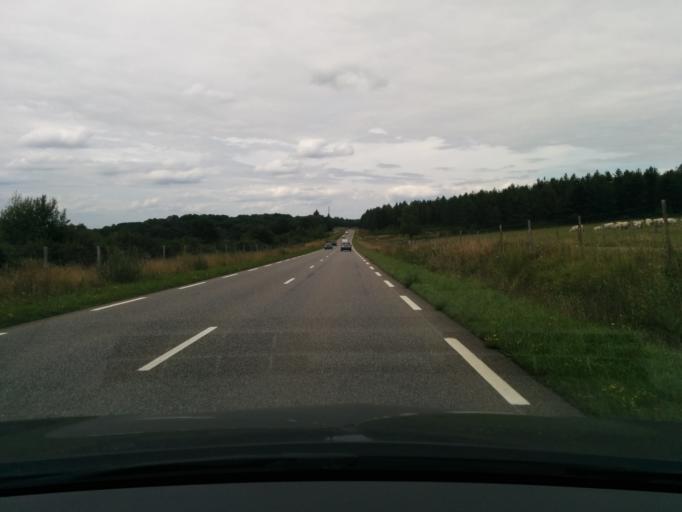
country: FR
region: Midi-Pyrenees
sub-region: Departement des Hautes-Pyrenees
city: La Barthe-de-Neste
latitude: 43.0572
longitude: 0.3606
